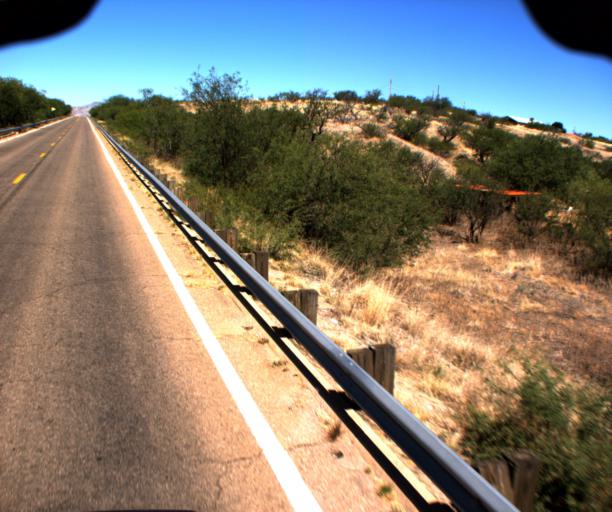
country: US
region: Arizona
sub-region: Santa Cruz County
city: Rio Rico
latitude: 31.4297
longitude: -110.9842
